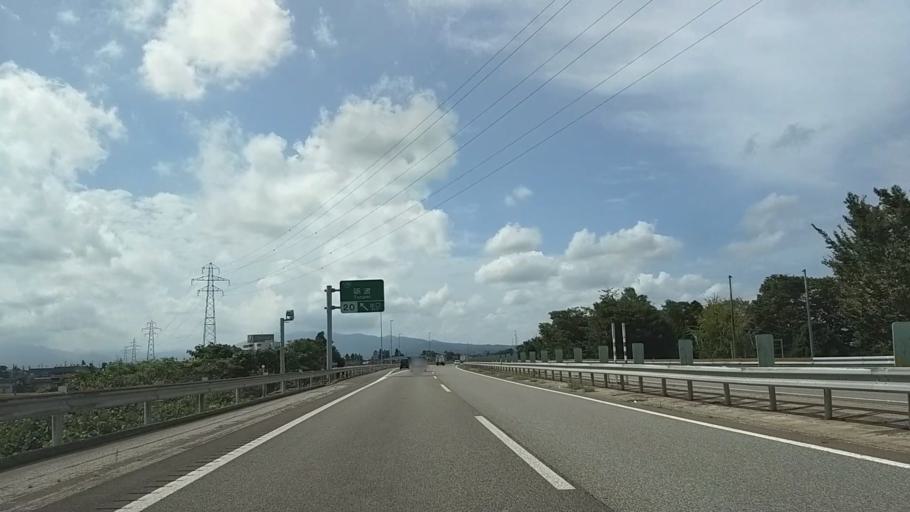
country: JP
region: Toyama
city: Nanto-shi
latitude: 36.6255
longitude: 136.9579
